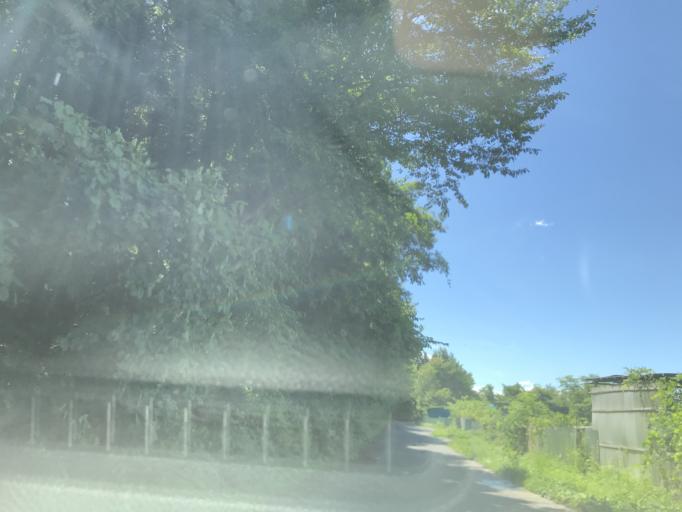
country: JP
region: Iwate
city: Ichinoseki
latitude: 38.9271
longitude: 141.0498
